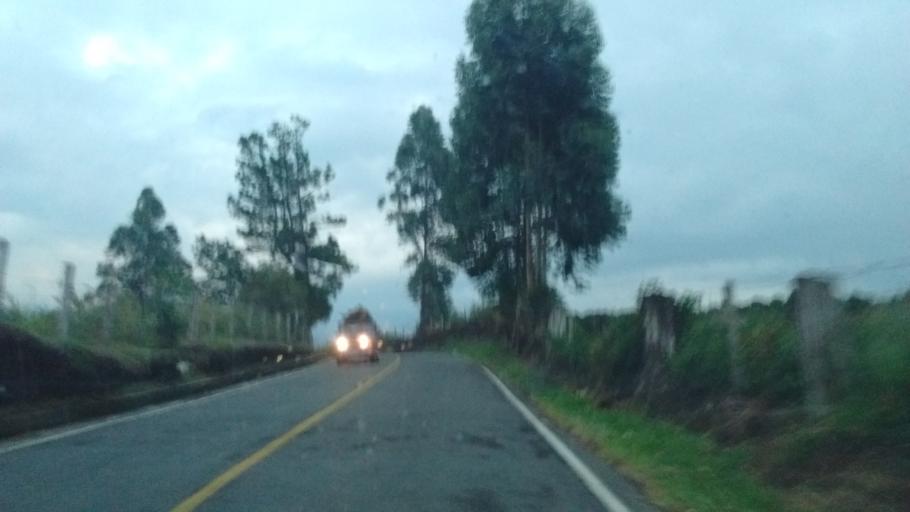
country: CO
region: Cauca
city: Popayan
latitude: 2.3686
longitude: -76.6934
